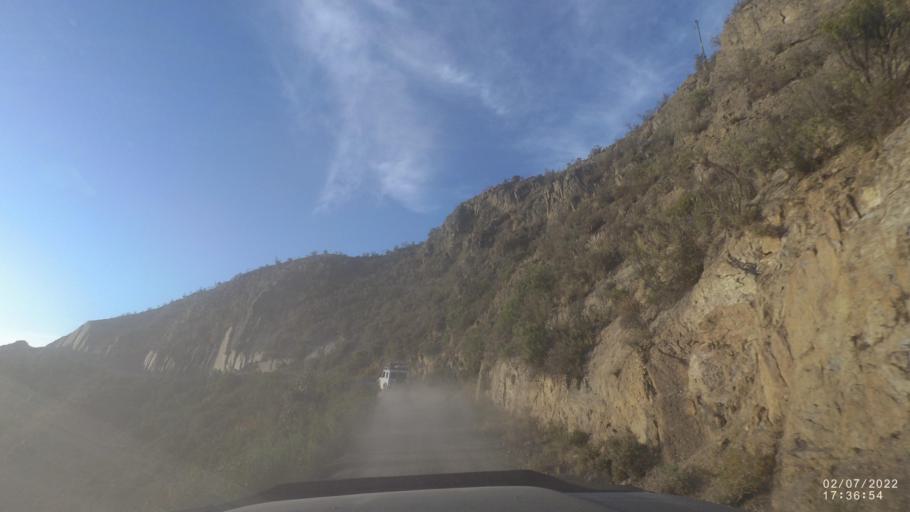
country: BO
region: Cochabamba
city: Irpa Irpa
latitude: -17.8745
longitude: -66.6191
